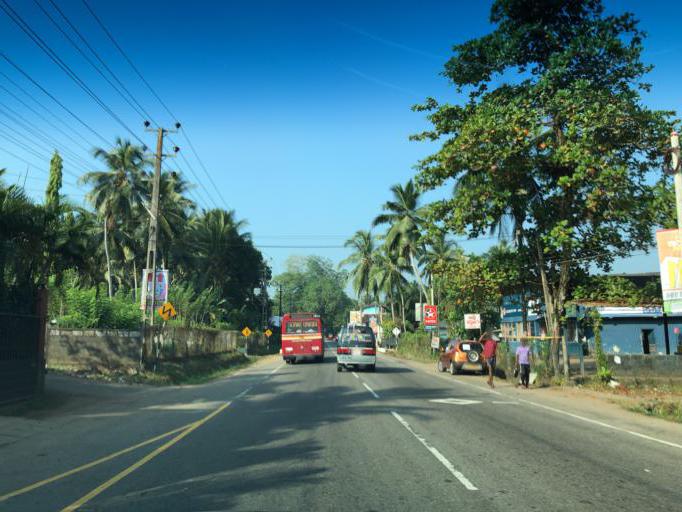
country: LK
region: Western
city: Horana South
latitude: 6.7304
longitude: 80.0998
